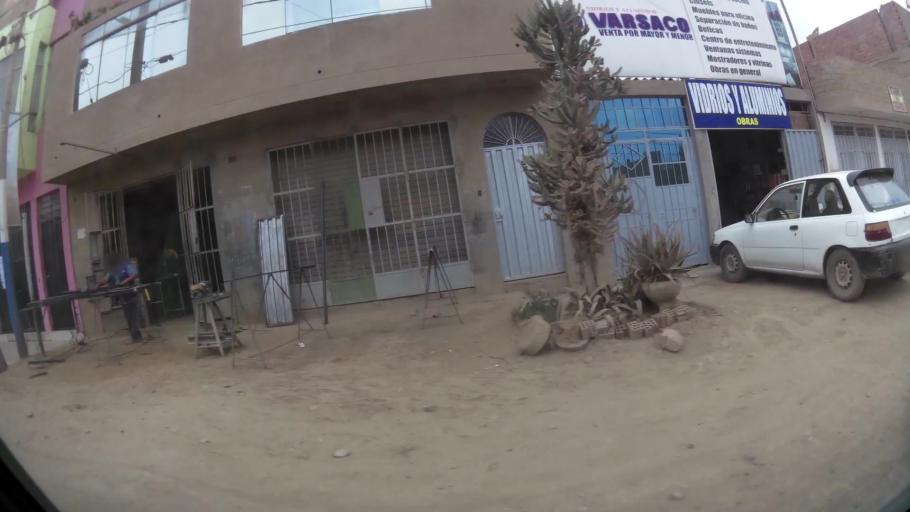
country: PE
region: Lima
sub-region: Lima
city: Independencia
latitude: -11.9599
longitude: -77.0977
